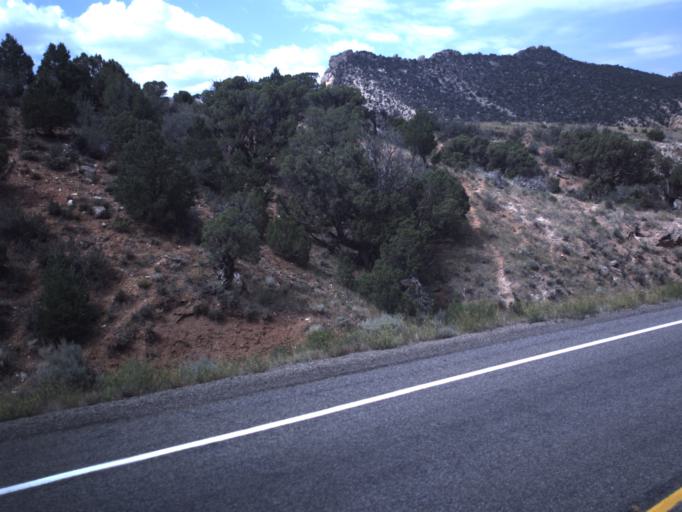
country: US
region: Utah
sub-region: Daggett County
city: Manila
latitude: 40.9329
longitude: -109.7146
